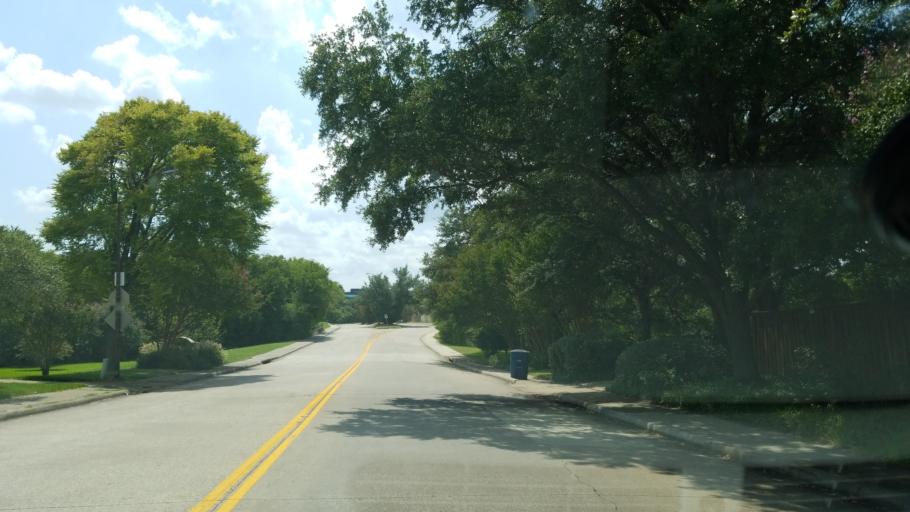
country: US
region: Texas
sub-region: Dallas County
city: Richardson
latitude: 32.9156
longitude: -96.7288
